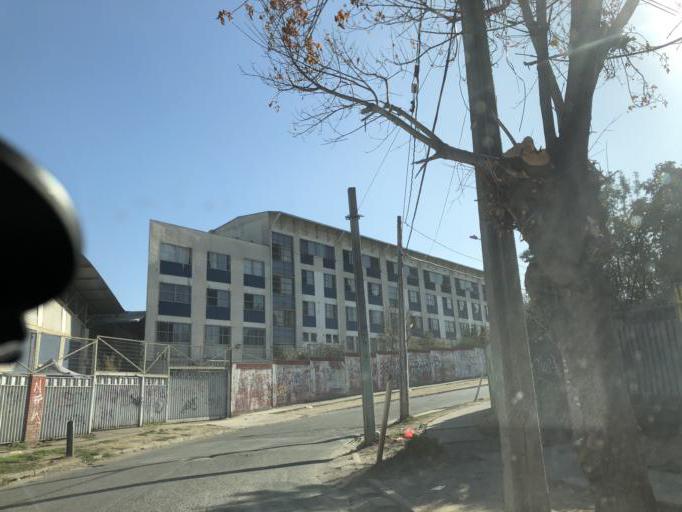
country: CL
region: Santiago Metropolitan
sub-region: Provincia de Cordillera
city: Puente Alto
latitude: -33.6258
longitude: -70.5920
